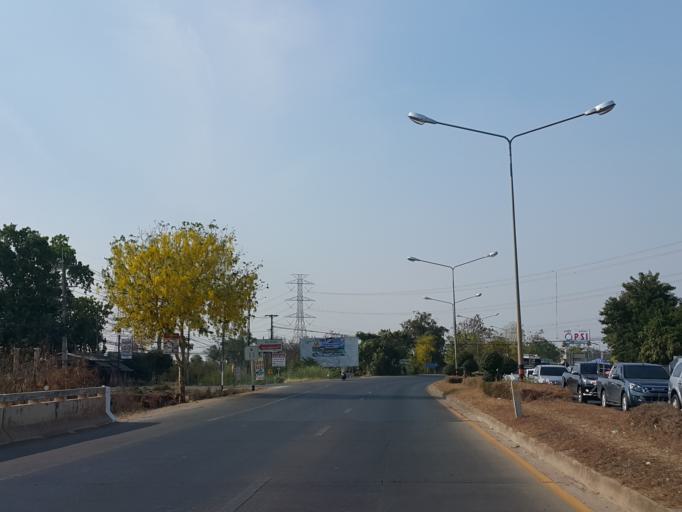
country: TH
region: Phitsanulok
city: Phitsanulok
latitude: 16.8202
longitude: 100.3308
